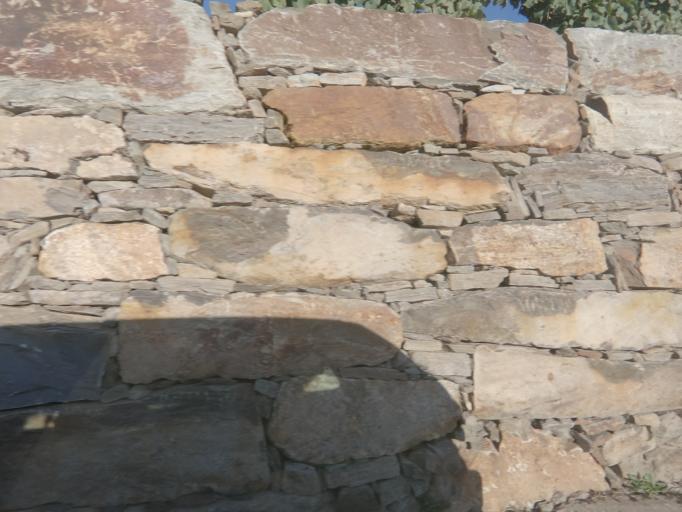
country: PT
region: Vila Real
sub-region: Peso da Regua
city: Godim
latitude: 41.1660
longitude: -7.8300
